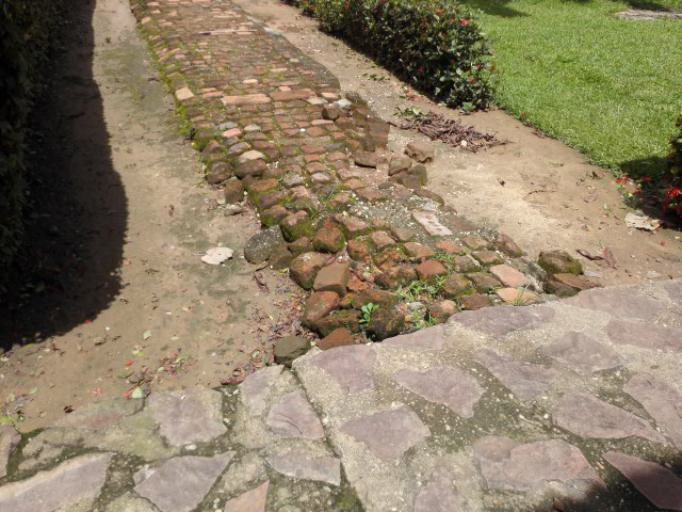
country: CD
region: Eastern Province
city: Kisangani
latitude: 0.5109
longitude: 25.2066
